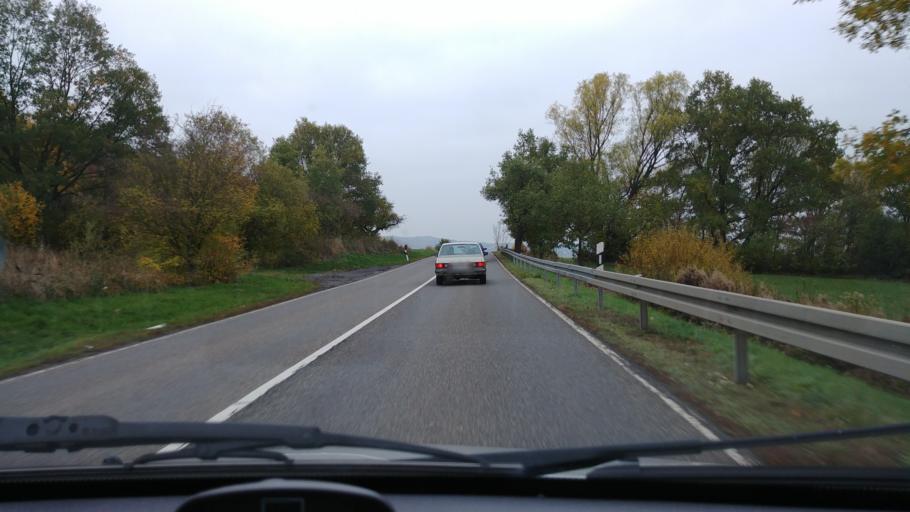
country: DE
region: Rheinland-Pfalz
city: Irmtraut
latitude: 50.5244
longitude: 8.0530
